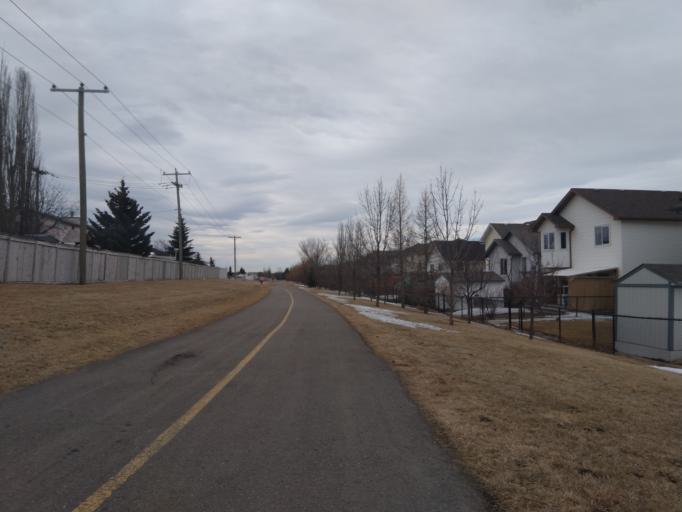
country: CA
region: Alberta
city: Calgary
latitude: 51.1605
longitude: -114.0481
